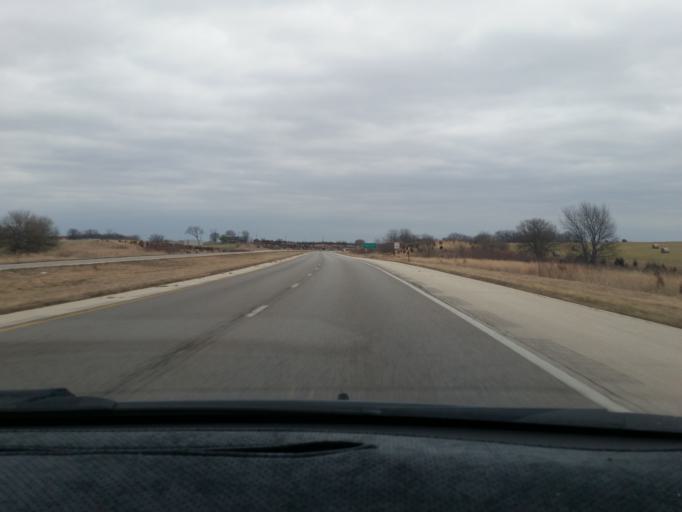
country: US
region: Kansas
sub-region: Johnson County
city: De Soto
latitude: 38.9504
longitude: -95.0296
